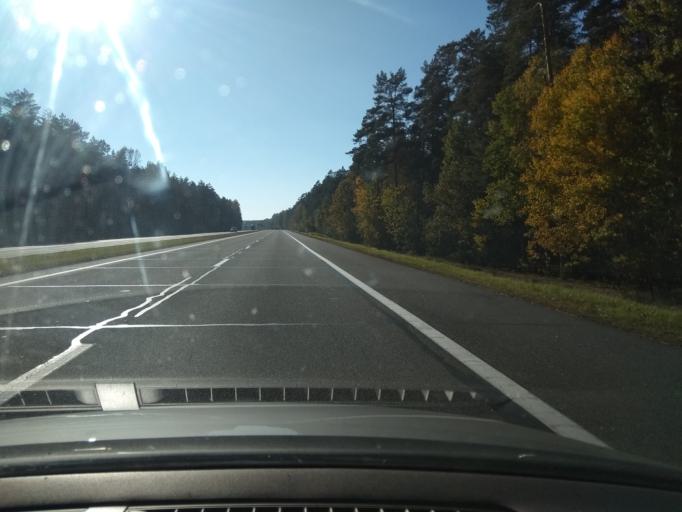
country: BY
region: Brest
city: Baranovichi
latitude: 53.0315
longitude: 25.8060
